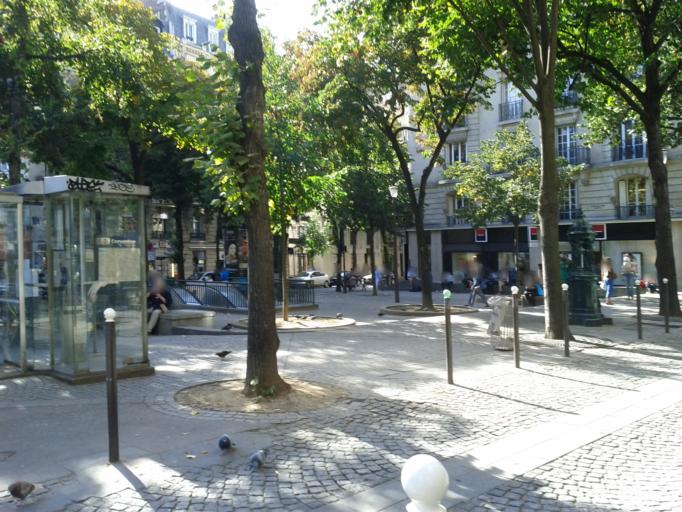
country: FR
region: Ile-de-France
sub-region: Departement des Hauts-de-Seine
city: Vanves
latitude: 48.8375
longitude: 2.2968
